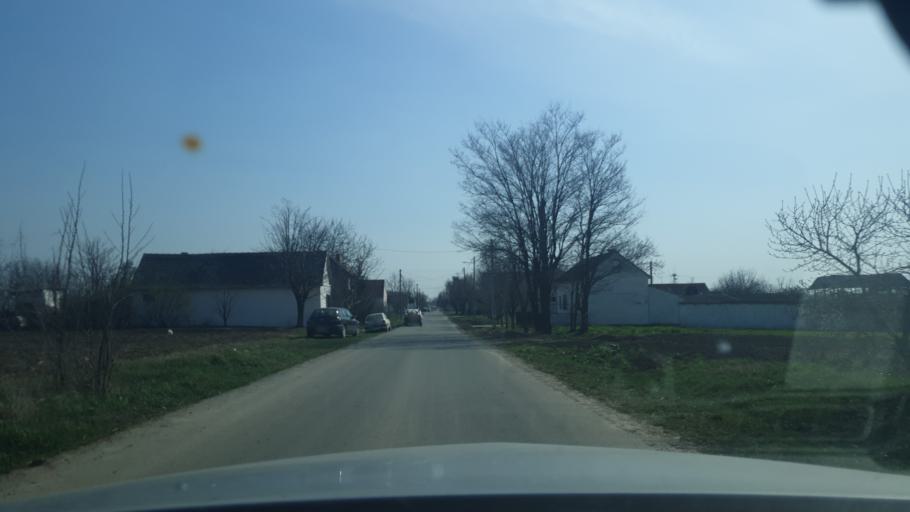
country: RS
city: Putinci
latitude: 45.0436
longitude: 19.9395
